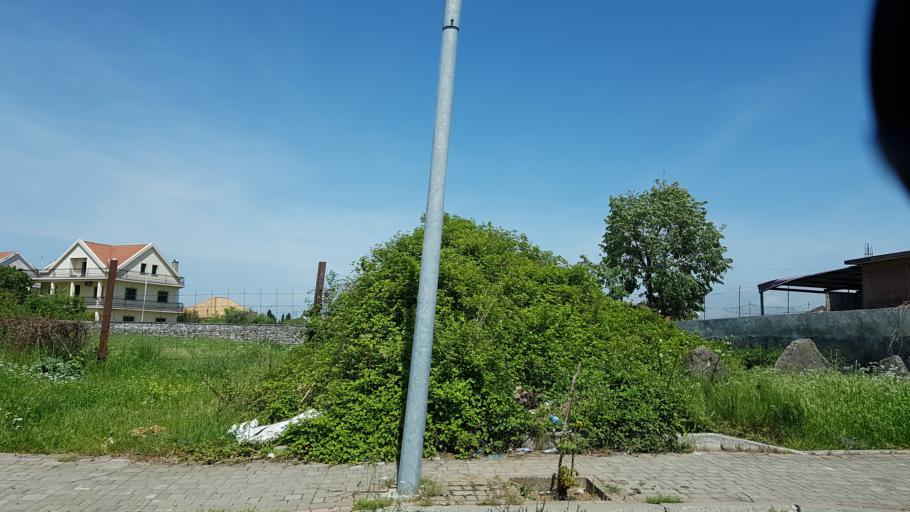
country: AL
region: Shkoder
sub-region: Rrethi i Shkodres
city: Shkoder
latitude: 42.0965
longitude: 19.5390
